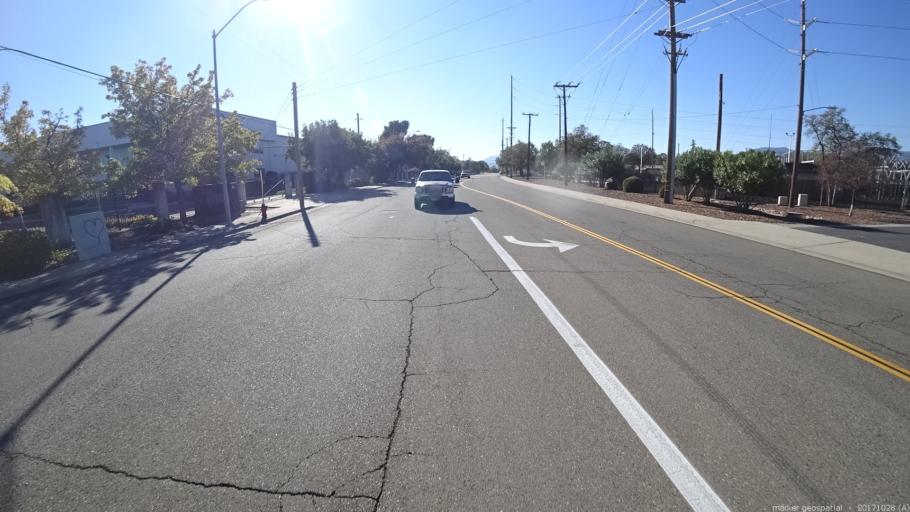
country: US
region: California
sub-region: Shasta County
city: Redding
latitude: 40.6332
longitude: -122.3912
